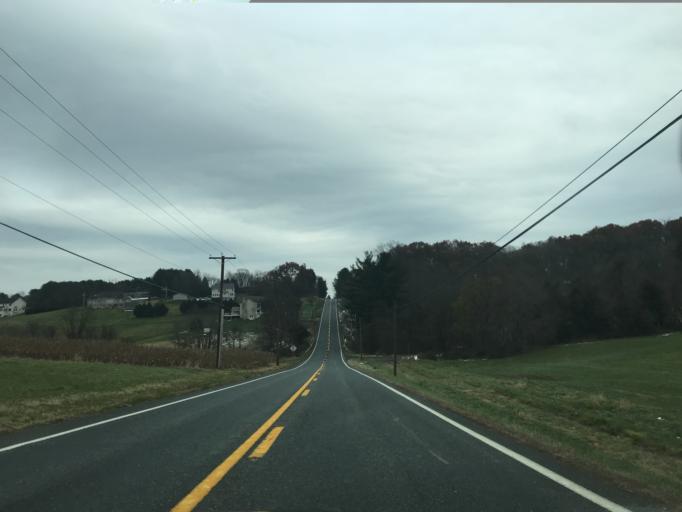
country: US
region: Pennsylvania
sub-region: York County
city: Susquehanna Trails
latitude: 39.6789
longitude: -76.3683
